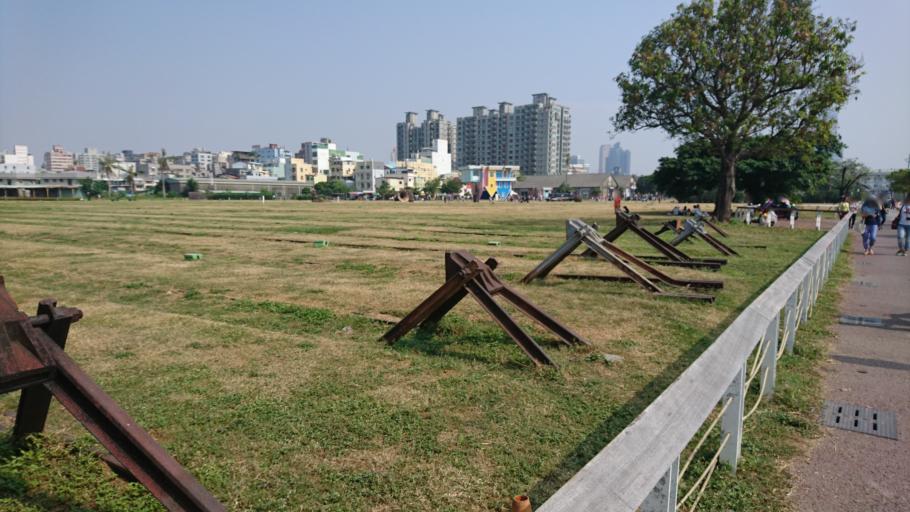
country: TW
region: Kaohsiung
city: Kaohsiung
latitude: 22.6210
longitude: 120.2757
